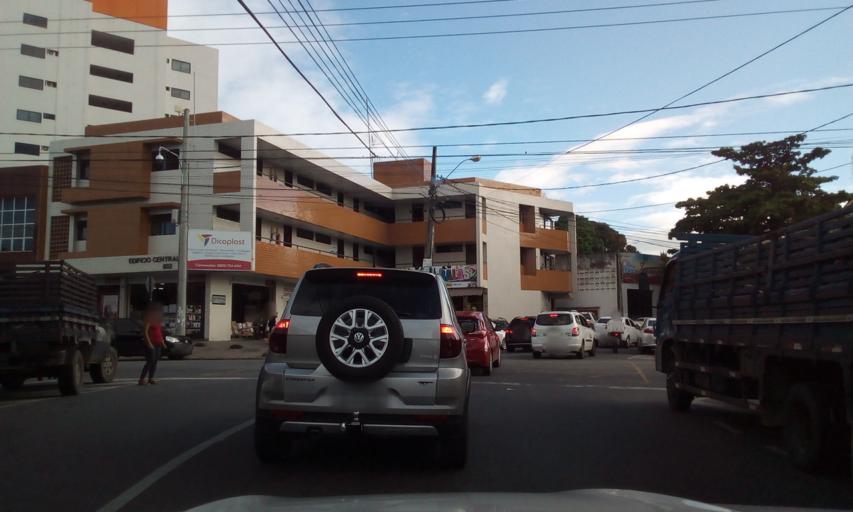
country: BR
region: Paraiba
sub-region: Joao Pessoa
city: Joao Pessoa
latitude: -7.1246
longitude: -34.8794
